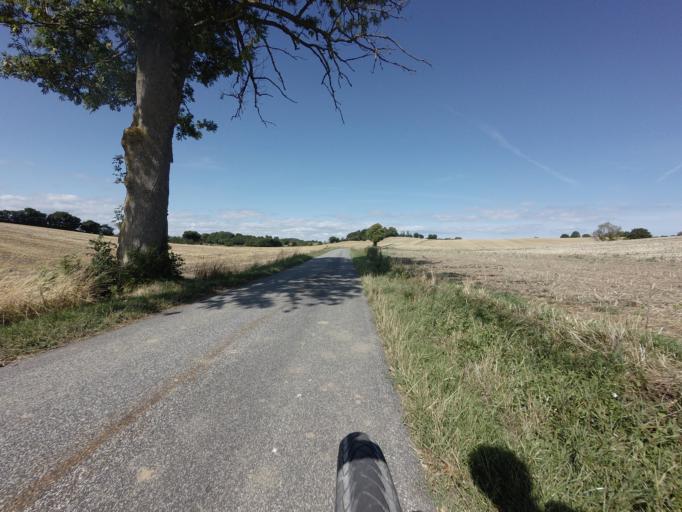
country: DK
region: Zealand
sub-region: Vordingborg Kommune
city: Stege
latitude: 55.0036
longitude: 12.4765
